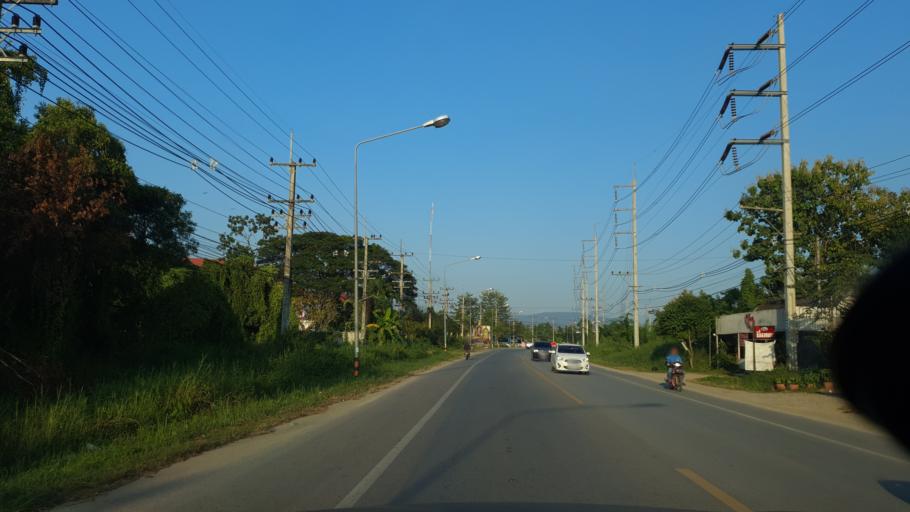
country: TH
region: Chiang Mai
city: San Sai
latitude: 18.9149
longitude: 98.9598
